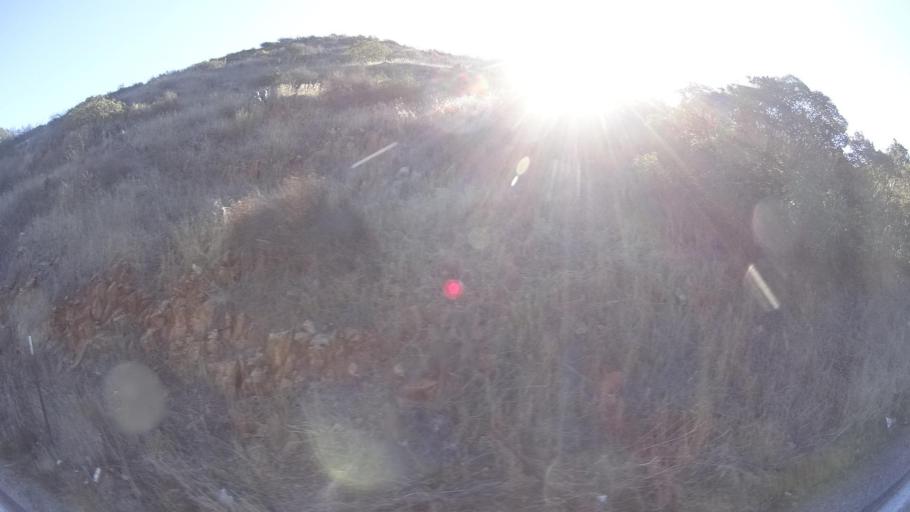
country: US
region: California
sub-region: San Diego County
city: Jamul
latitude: 32.6447
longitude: -116.8699
